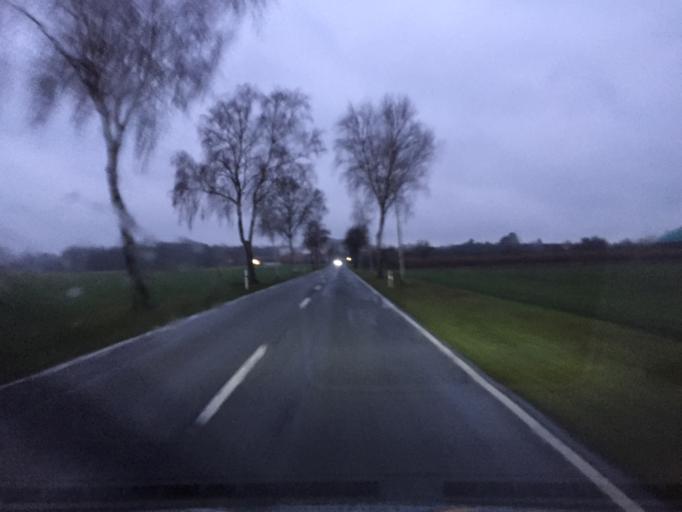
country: DE
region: Lower Saxony
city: Sudwalde
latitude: 52.8017
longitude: 8.8425
